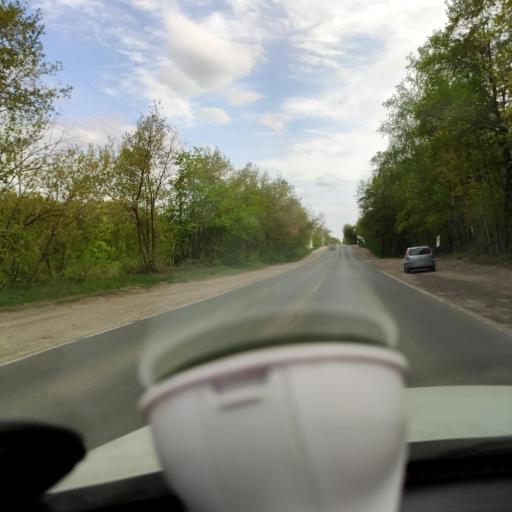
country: RU
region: Samara
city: Petra-Dubrava
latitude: 53.3160
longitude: 50.2705
